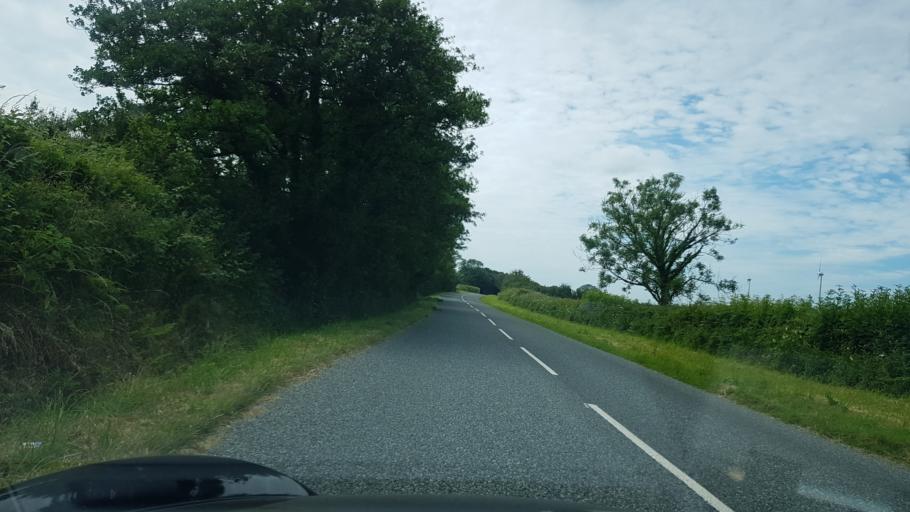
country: GB
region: Wales
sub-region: Pembrokeshire
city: Kilgetty
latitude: 51.7717
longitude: -4.6650
